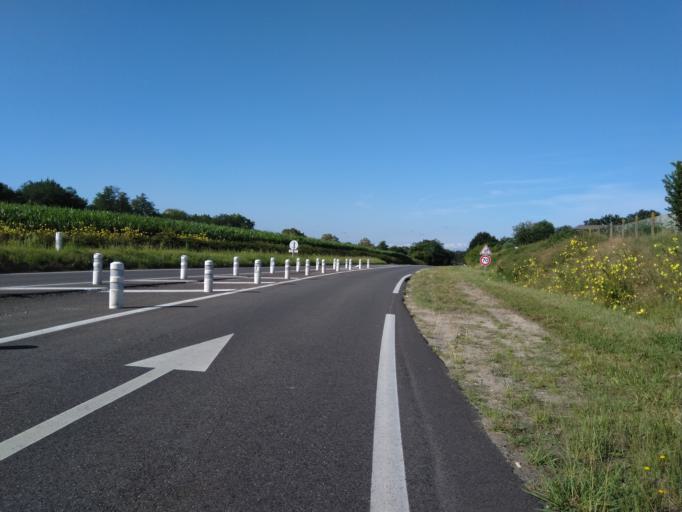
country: FR
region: Aquitaine
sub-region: Departement des Landes
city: Saint-Vincent-de-Paul
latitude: 43.7362
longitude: -1.0271
